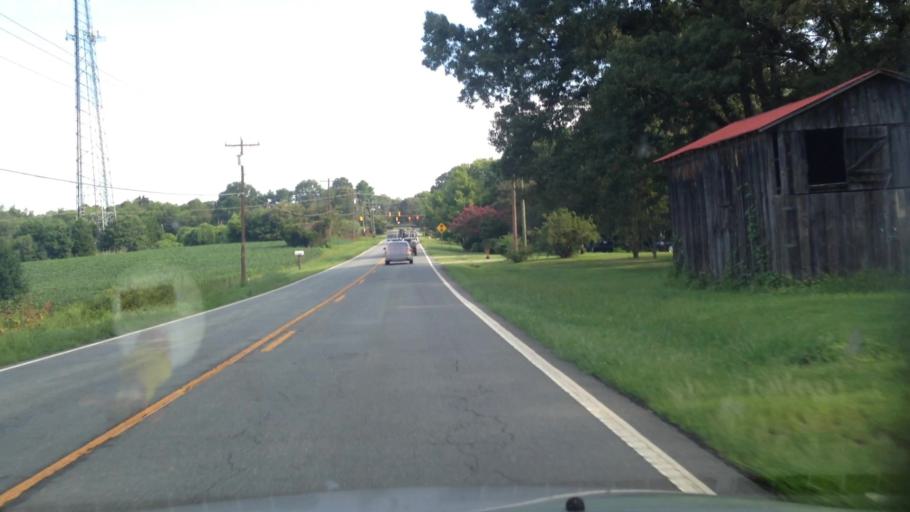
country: US
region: North Carolina
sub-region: Guilford County
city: Oak Ridge
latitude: 36.2151
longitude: -80.0567
